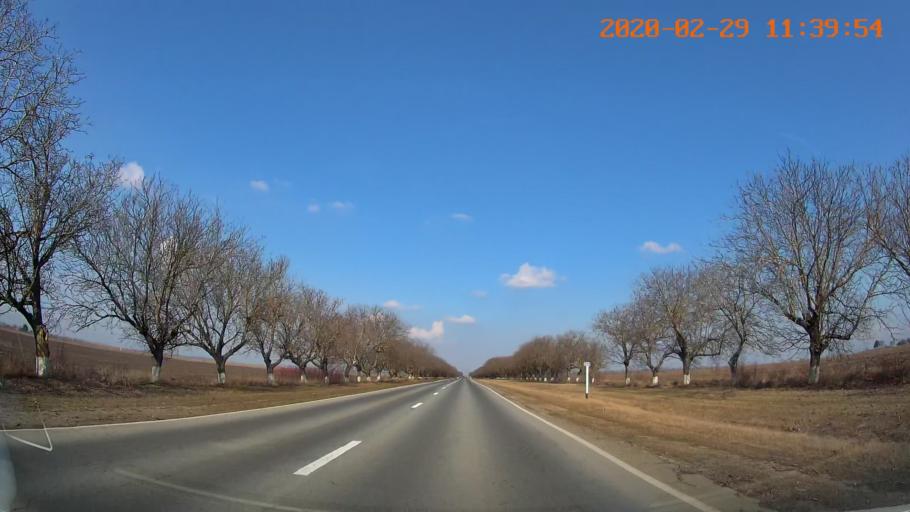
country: MD
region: Rezina
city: Saharna
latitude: 47.6476
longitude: 29.0224
